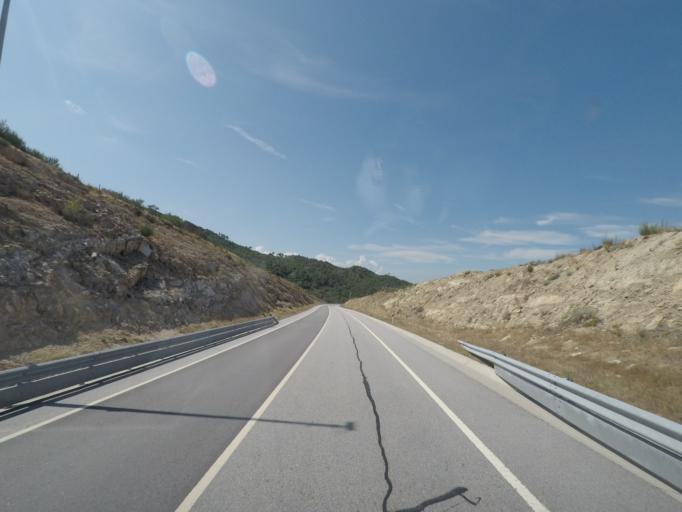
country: PT
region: Braganca
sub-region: Carrazeda de Ansiaes
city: Carrazeda de Anciaes
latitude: 41.2713
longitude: -7.3069
